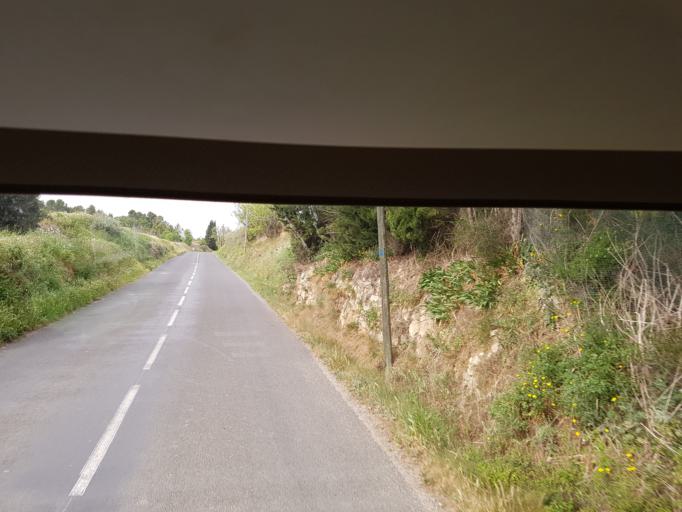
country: FR
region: Languedoc-Roussillon
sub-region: Departement de l'Aude
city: Fleury
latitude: 43.2227
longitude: 3.1322
